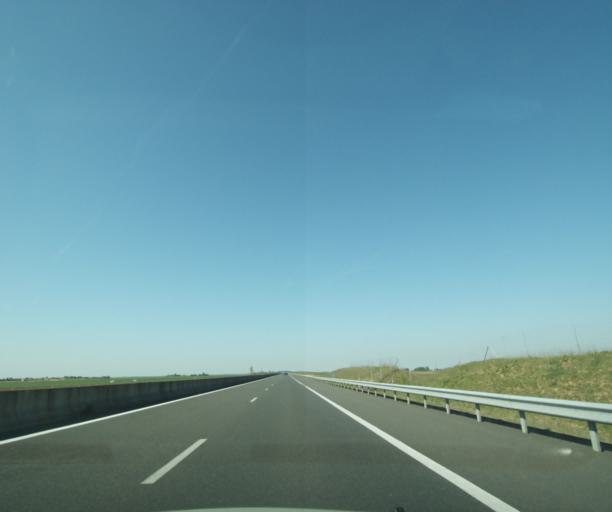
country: FR
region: Centre
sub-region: Departement du Loiret
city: Ascheres-le-Marche
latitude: 48.0868
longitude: 2.0008
